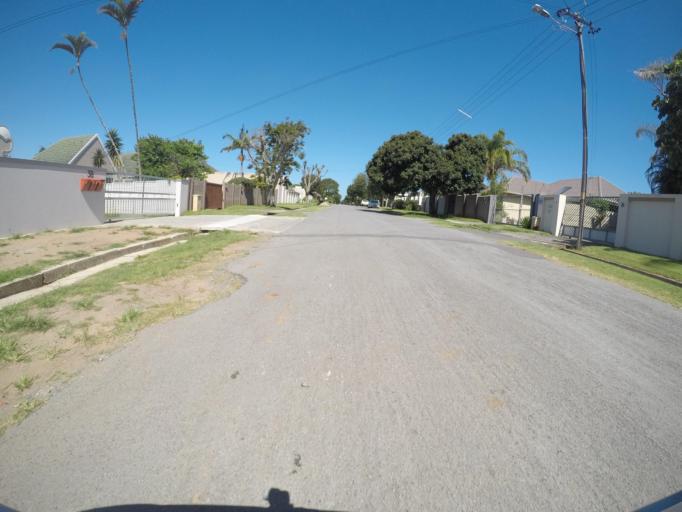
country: ZA
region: Eastern Cape
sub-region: Buffalo City Metropolitan Municipality
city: East London
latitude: -32.9865
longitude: 27.9339
